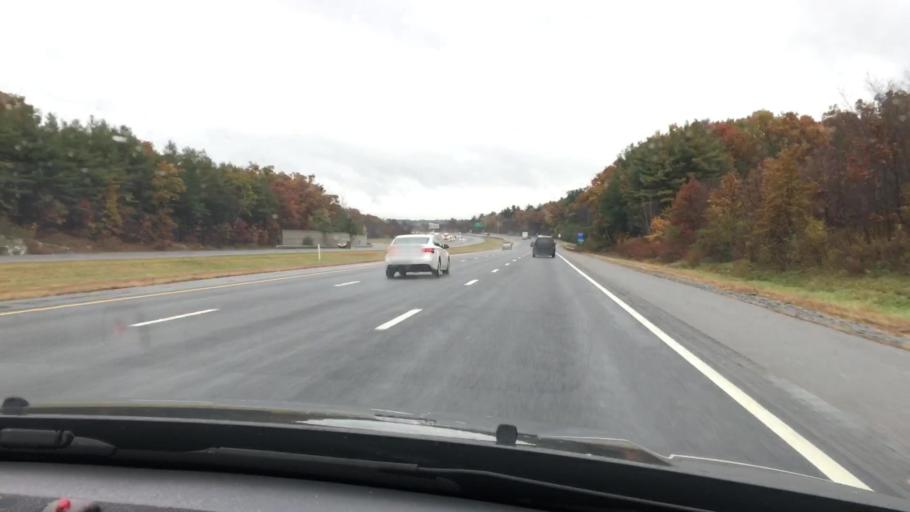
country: US
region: Massachusetts
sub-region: Middlesex County
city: Tyngsboro
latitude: 42.6366
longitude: -71.4103
